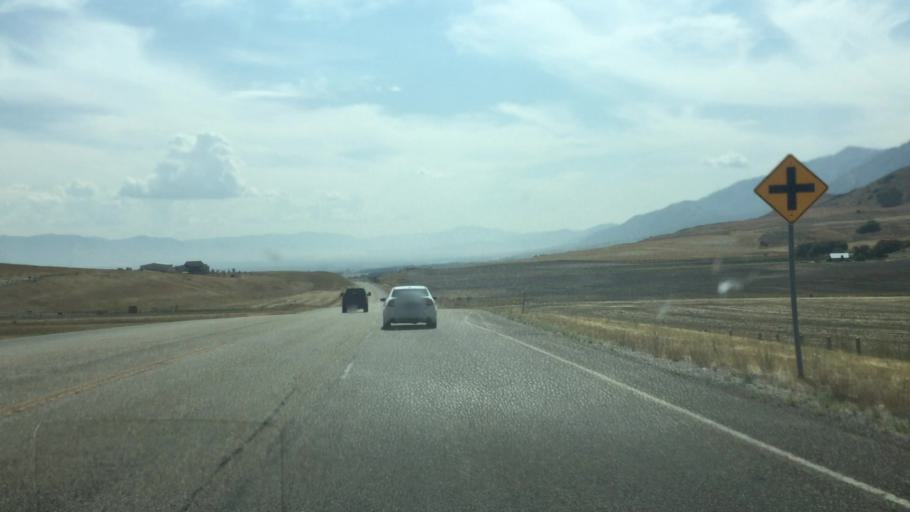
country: US
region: Utah
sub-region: Cache County
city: Mendon
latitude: 41.7777
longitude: -112.0212
